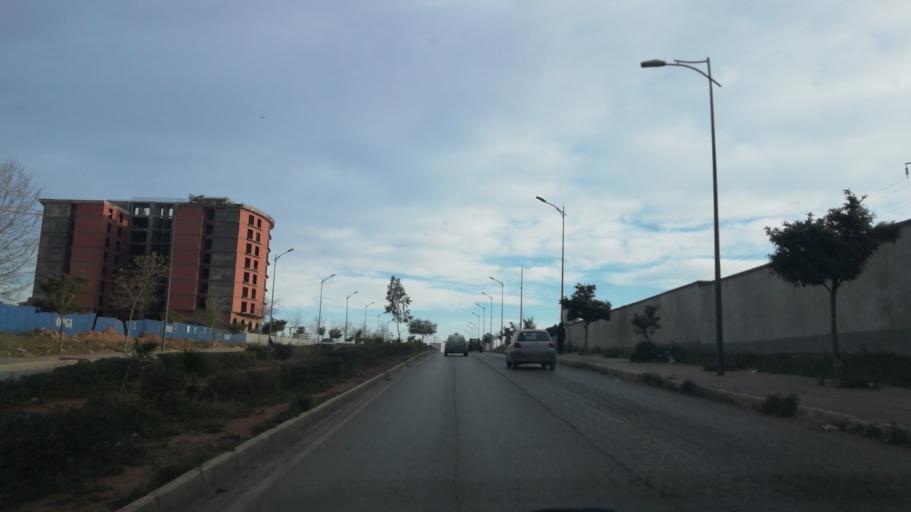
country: DZ
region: Oran
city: Bir el Djir
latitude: 35.7089
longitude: -0.5737
